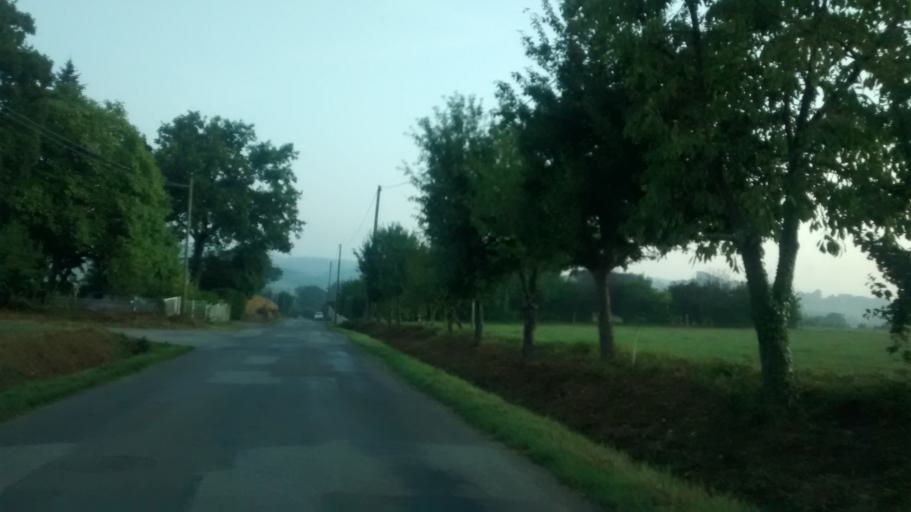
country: FR
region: Brittany
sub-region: Departement d'Ille-et-Vilaine
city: Montreuil-sous-Perouse
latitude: 48.1377
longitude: -1.2542
